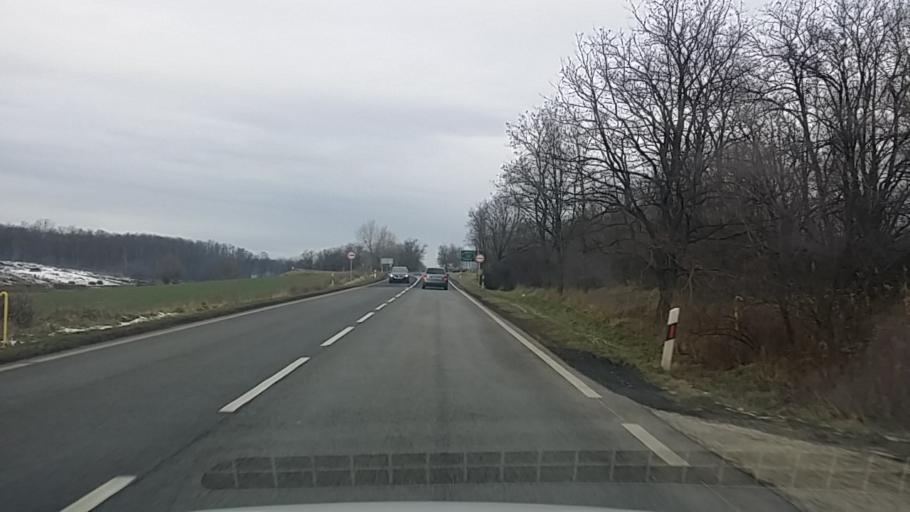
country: HU
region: Komarom-Esztergom
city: Kisber
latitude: 47.4830
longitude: 18.0666
